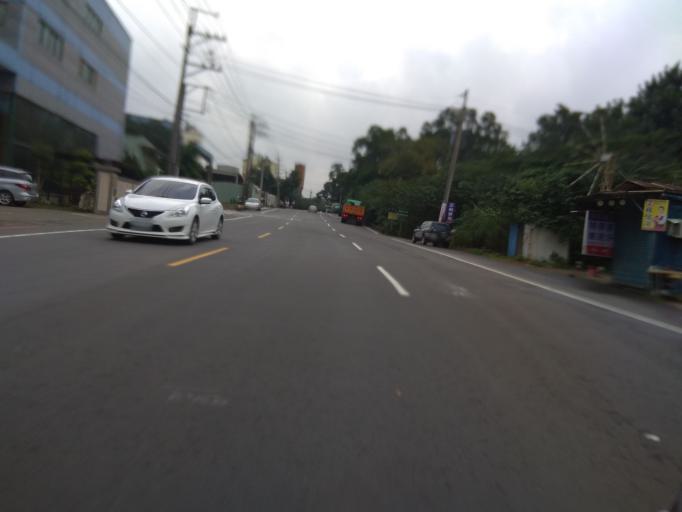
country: TW
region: Taiwan
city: Daxi
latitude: 24.9248
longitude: 121.1629
